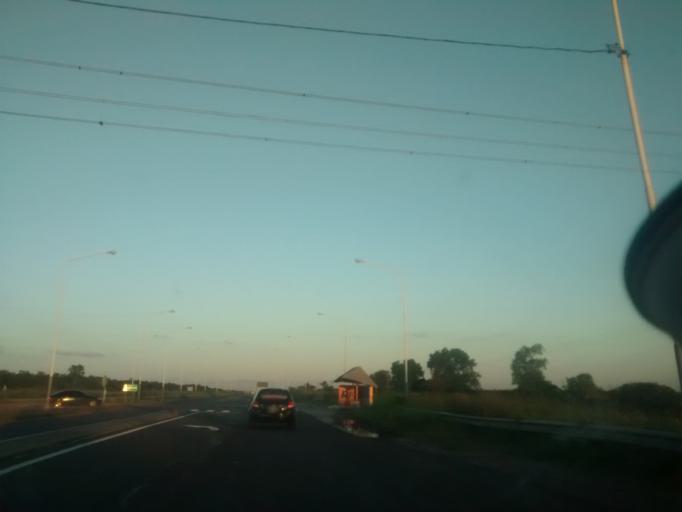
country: AR
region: Chaco
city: La Escondida
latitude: -27.1365
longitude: -59.4644
